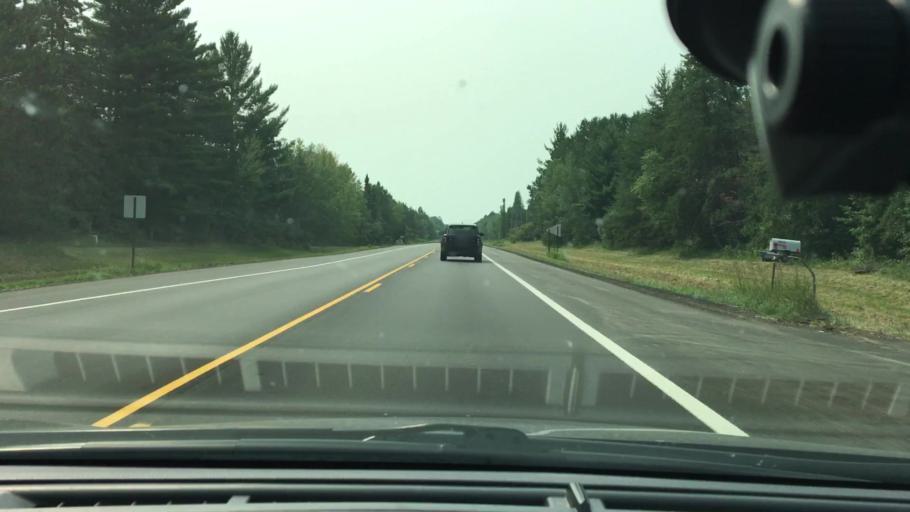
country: US
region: Minnesota
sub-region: Crow Wing County
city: Brainerd
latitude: 46.4491
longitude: -94.1720
